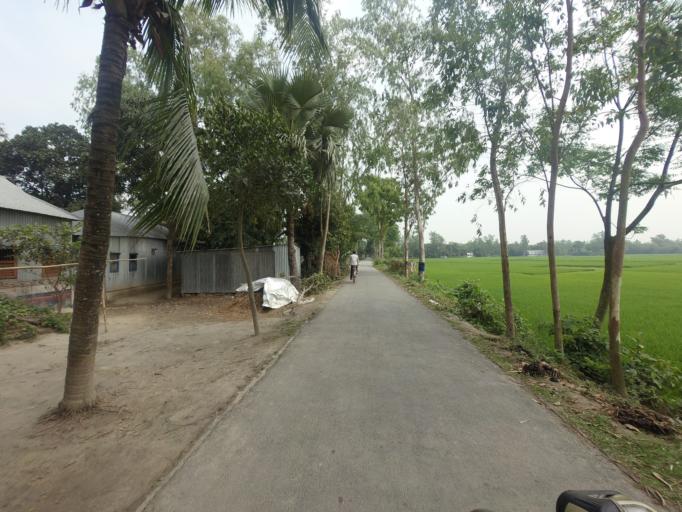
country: BD
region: Rajshahi
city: Sirajganj
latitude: 24.3265
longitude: 89.6768
